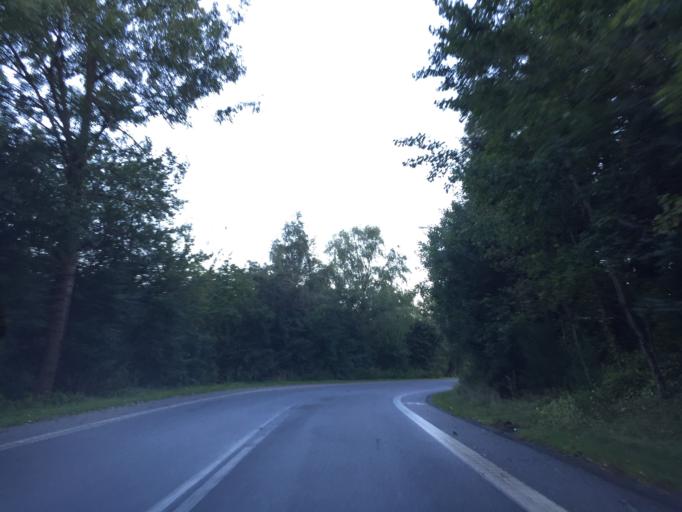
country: DK
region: Central Jutland
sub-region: Viborg Kommune
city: Bjerringbro
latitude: 56.3624
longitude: 9.6634
